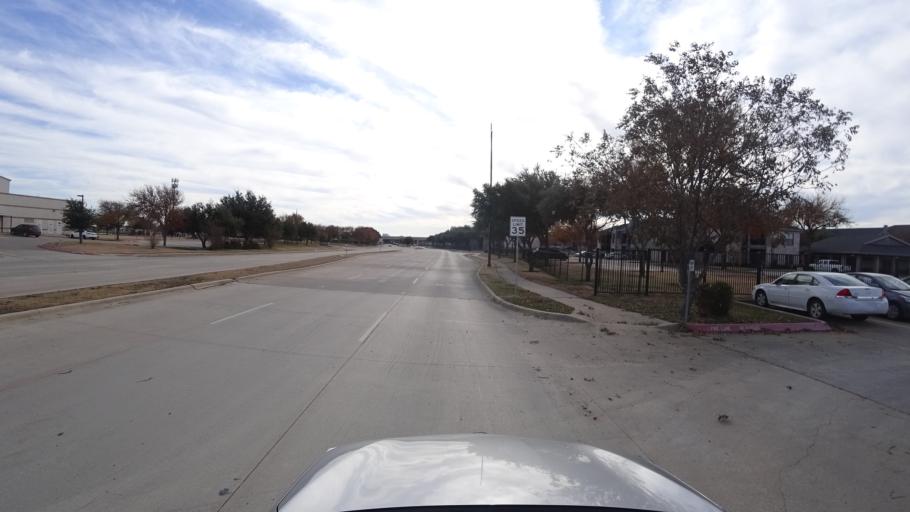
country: US
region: Texas
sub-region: Denton County
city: Lewisville
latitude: 33.0144
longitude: -96.9458
